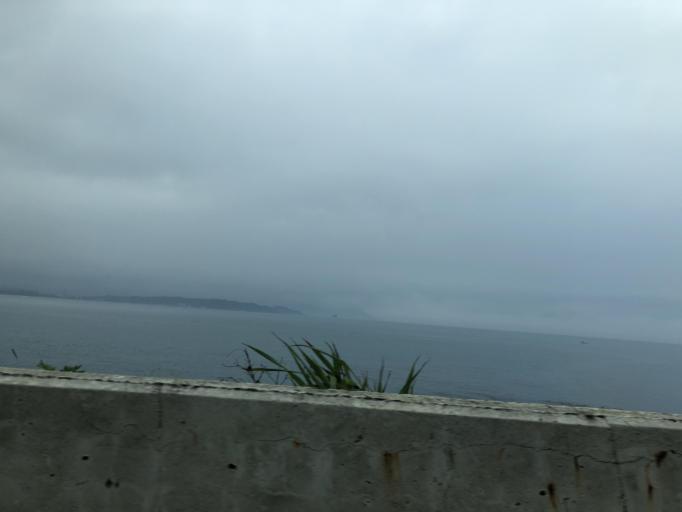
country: TW
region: Taiwan
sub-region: Keelung
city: Keelung
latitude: 25.2058
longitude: 121.6835
